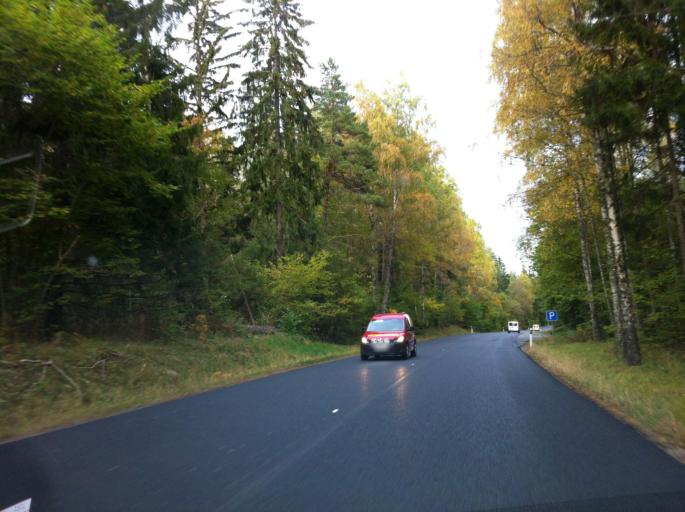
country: SE
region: OEstergoetland
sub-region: Motala Kommun
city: Ryd
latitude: 58.7070
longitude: 14.9629
